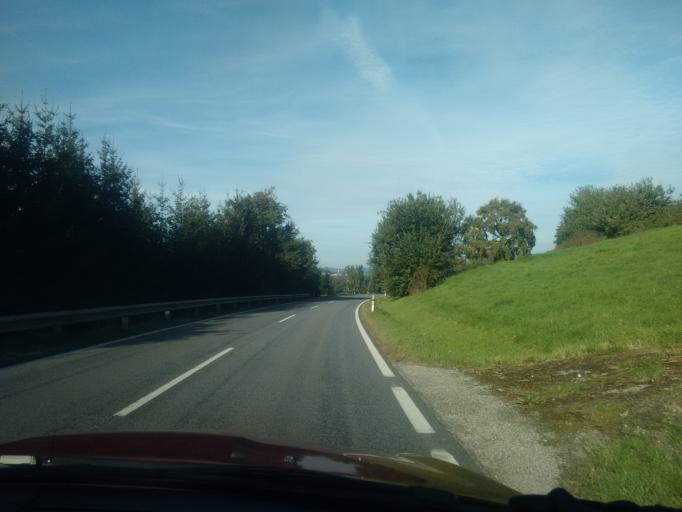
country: AT
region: Upper Austria
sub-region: Politischer Bezirk Vocklabruck
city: Rutzenham
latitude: 48.0667
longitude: 13.7089
